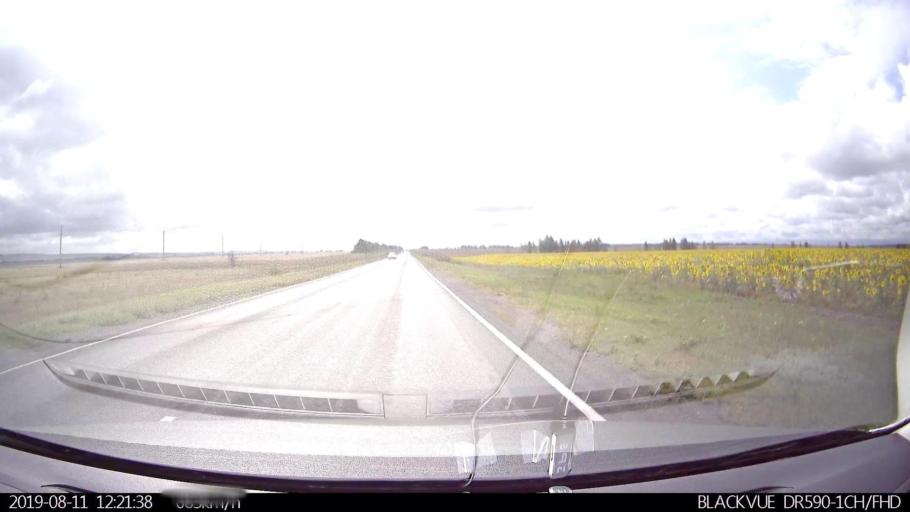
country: RU
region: Ulyanovsk
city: Ignatovka
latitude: 53.9185
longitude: 47.9572
